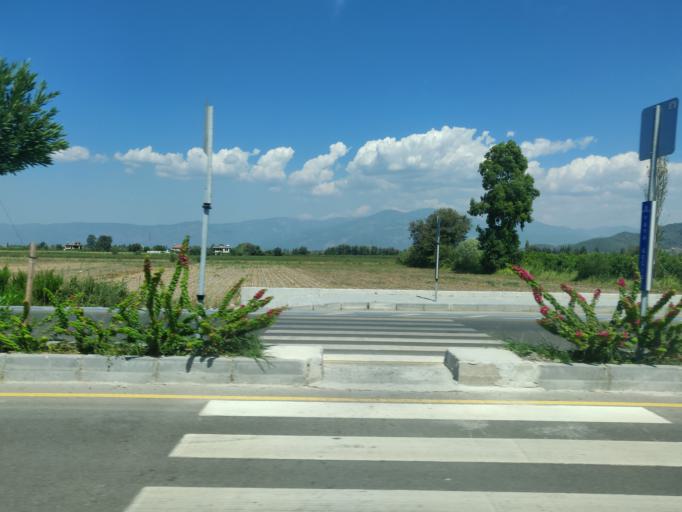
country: TR
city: Dalyan
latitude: 36.8386
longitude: 28.6610
